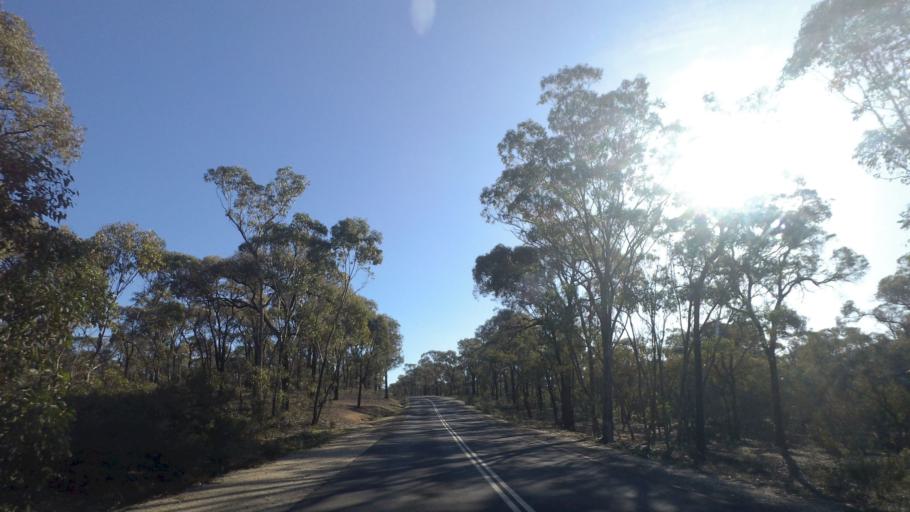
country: AU
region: Victoria
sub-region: Greater Bendigo
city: Kangaroo Flat
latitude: -36.8234
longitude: 144.2716
